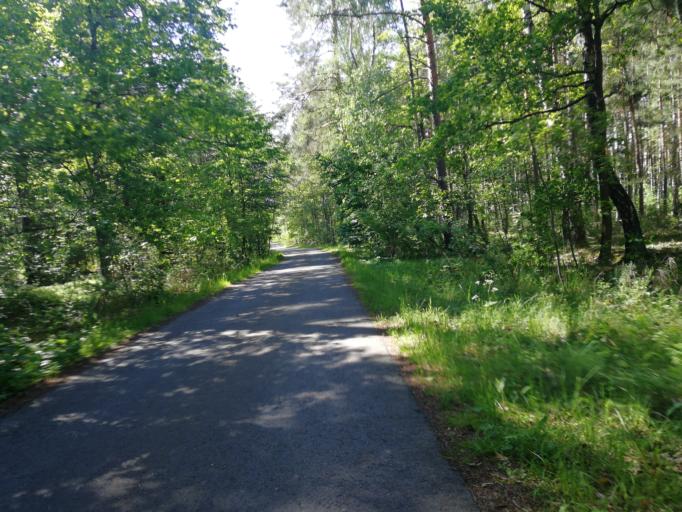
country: DE
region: Brandenburg
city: Calau
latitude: 51.7230
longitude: 13.9254
